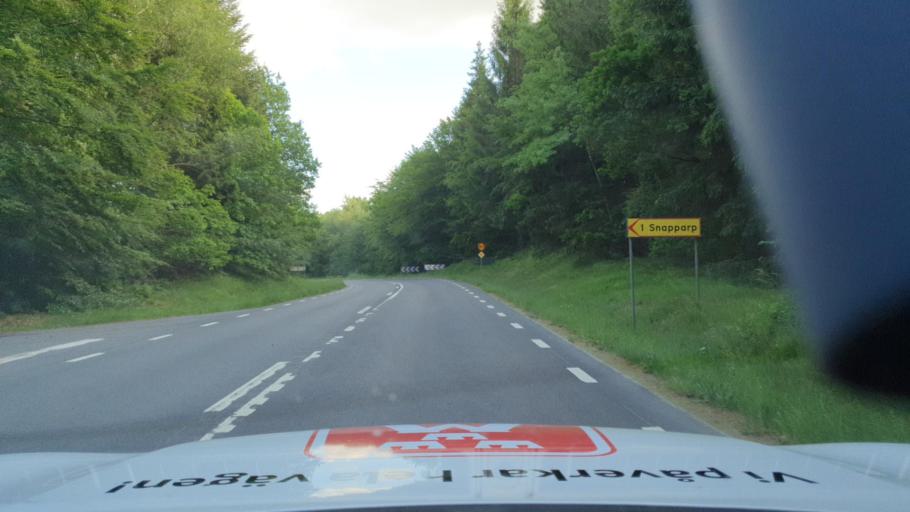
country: SE
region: Skane
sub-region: Simrishamns Kommun
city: Kivik
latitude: 55.6139
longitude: 14.1377
